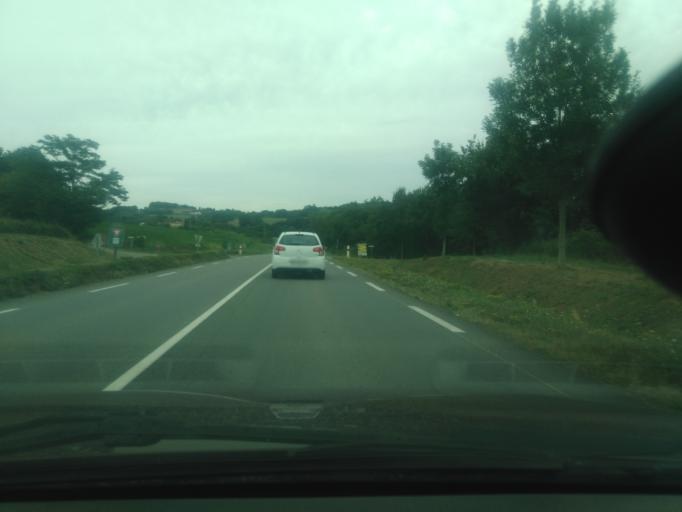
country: FR
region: Pays de la Loire
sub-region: Departement de la Vendee
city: Antigny
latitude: 46.6579
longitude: -0.7759
